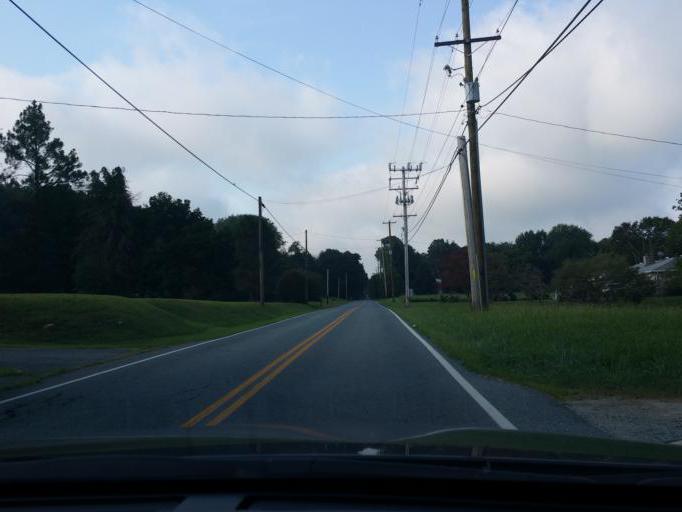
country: US
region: Maryland
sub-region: Cecil County
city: Rising Sun
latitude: 39.6507
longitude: -76.1230
